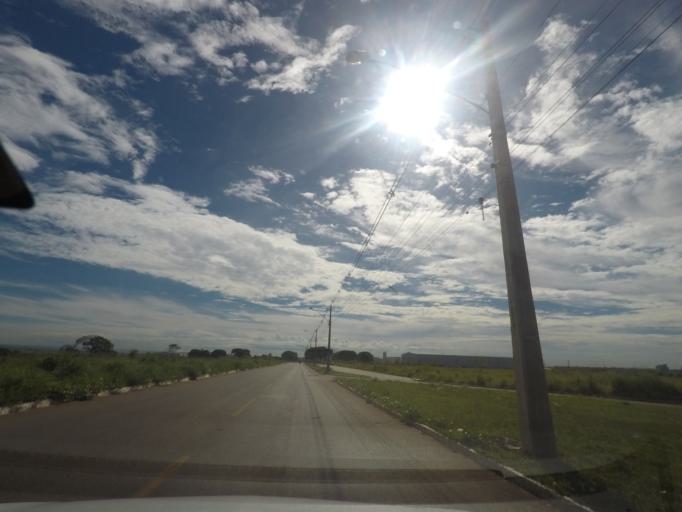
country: BR
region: Goias
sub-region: Aparecida De Goiania
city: Aparecida de Goiania
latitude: -16.8089
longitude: -49.2750
